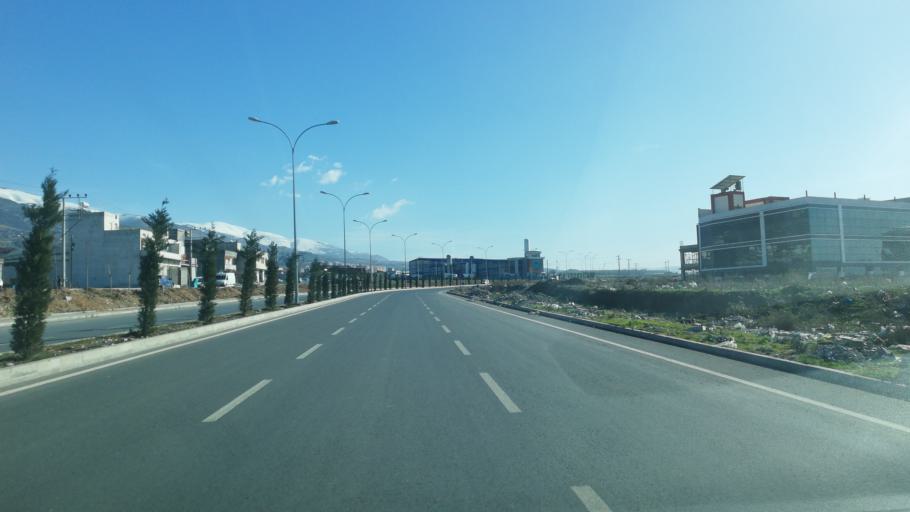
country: TR
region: Kahramanmaras
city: Kahramanmaras
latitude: 37.5707
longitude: 36.9661
